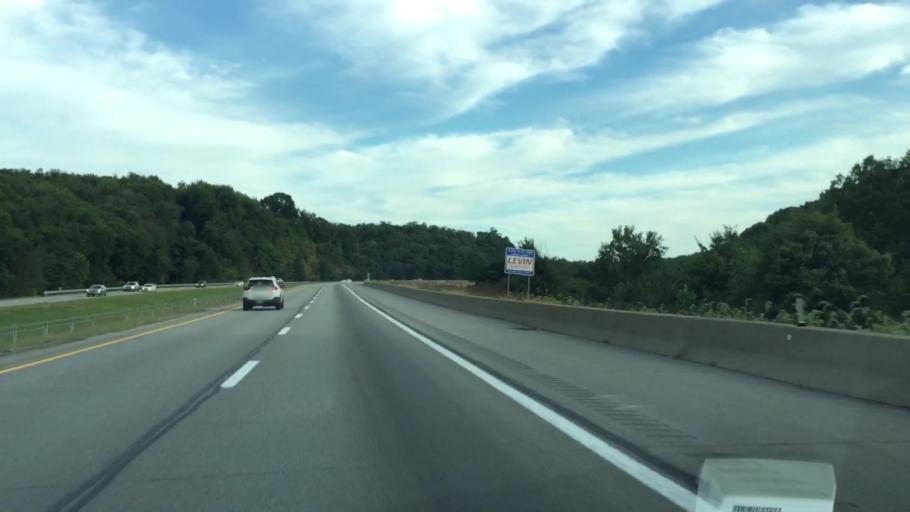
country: US
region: Pennsylvania
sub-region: Allegheny County
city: Franklin Park
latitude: 40.5735
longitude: -80.0923
